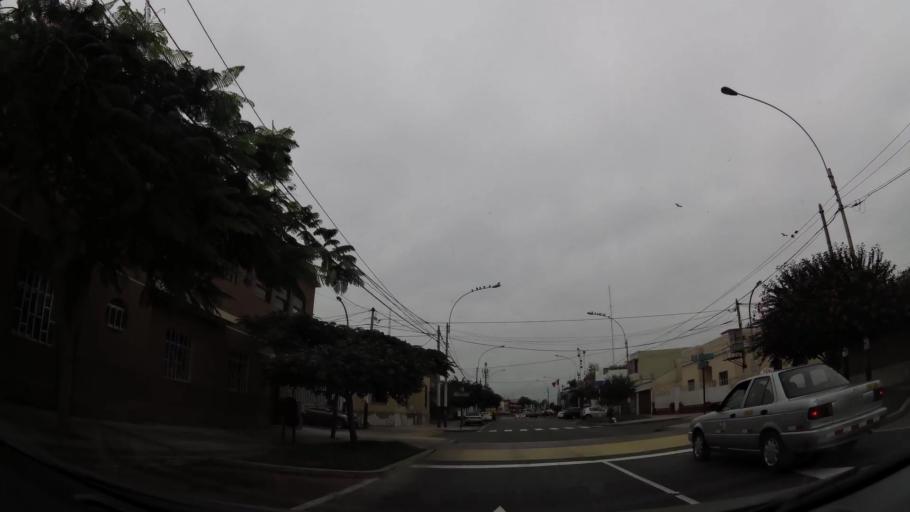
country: PE
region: Callao
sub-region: Callao
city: Callao
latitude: -12.0690
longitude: -77.1590
